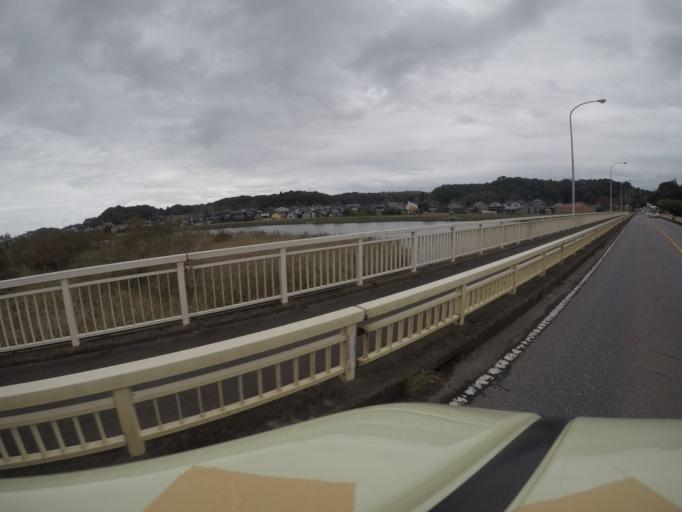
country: JP
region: Ibaraki
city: Inashiki
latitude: 35.9717
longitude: 140.3525
